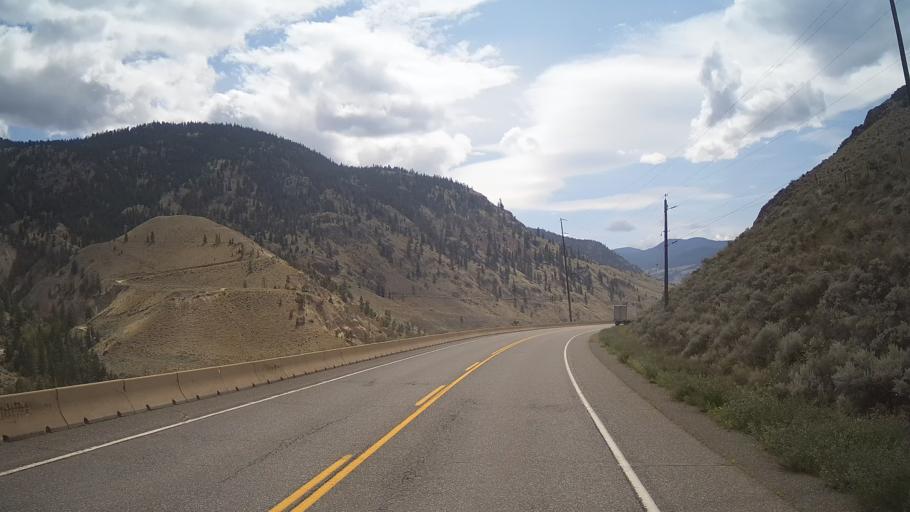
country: CA
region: British Columbia
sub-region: Thompson-Nicola Regional District
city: Ashcroft
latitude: 50.4687
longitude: -121.3001
